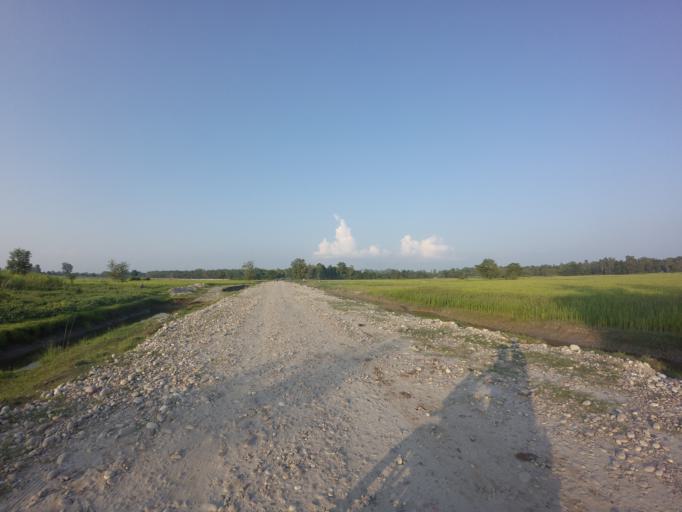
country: NP
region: Far Western
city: Tikapur
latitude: 28.4428
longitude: 81.0717
